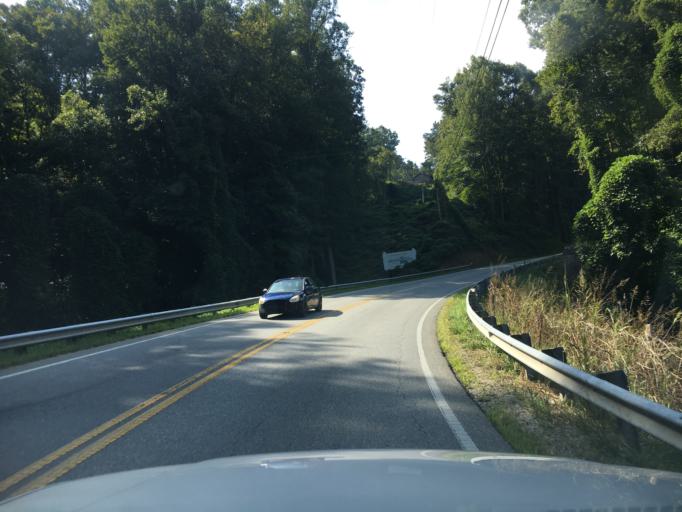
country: US
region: North Carolina
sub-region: Swain County
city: Bryson City
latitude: 35.3583
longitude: -83.5519
